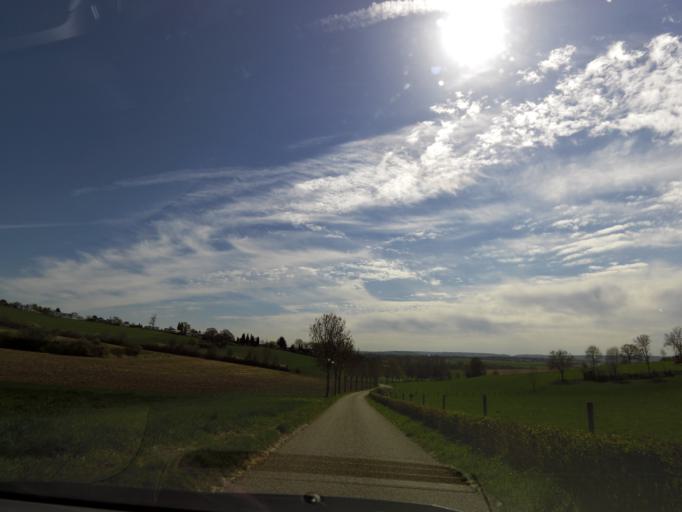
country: NL
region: Limburg
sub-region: Gemeente Simpelveld
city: Simpelveld
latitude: 50.8414
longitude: 5.9661
